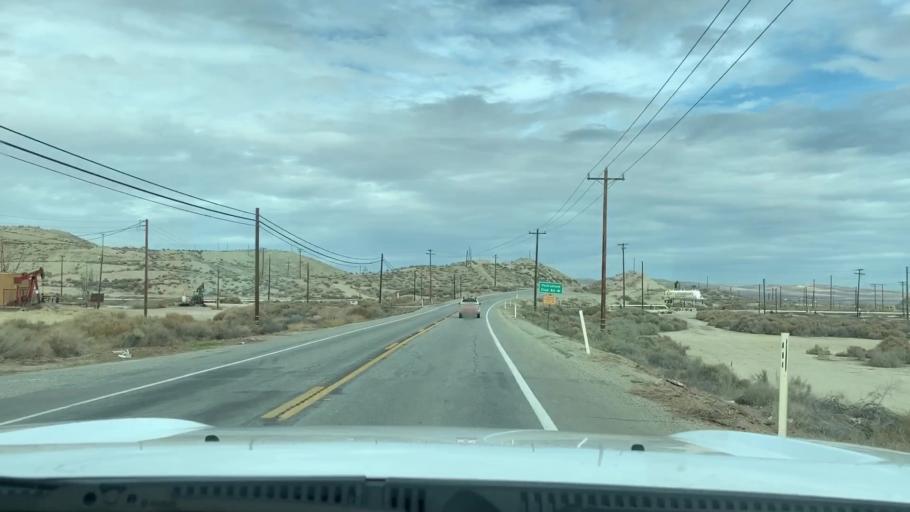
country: US
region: California
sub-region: Kern County
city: Maricopa
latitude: 35.0749
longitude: -119.4019
